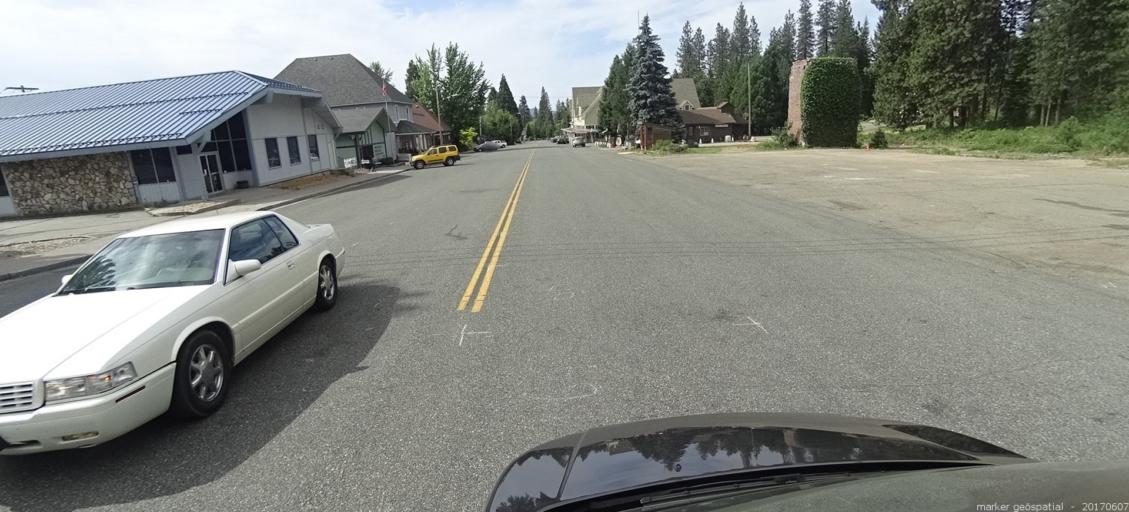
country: US
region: California
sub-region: Siskiyou County
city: McCloud
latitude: 41.2547
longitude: -122.1395
